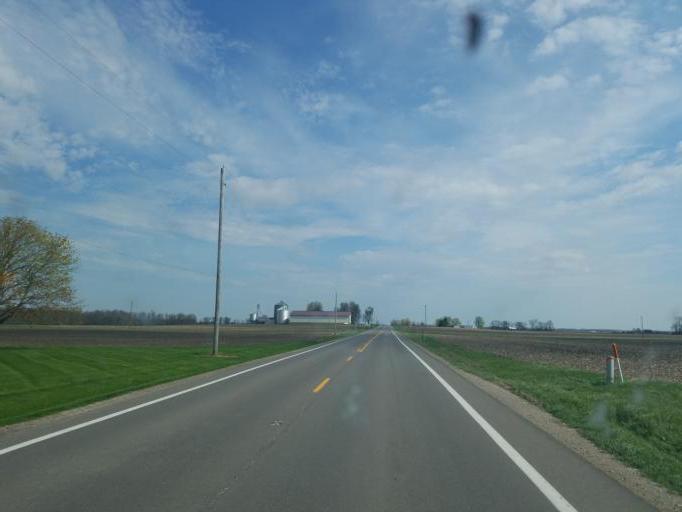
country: US
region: Ohio
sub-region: Crawford County
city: Bucyrus
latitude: 40.7449
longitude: -82.9923
